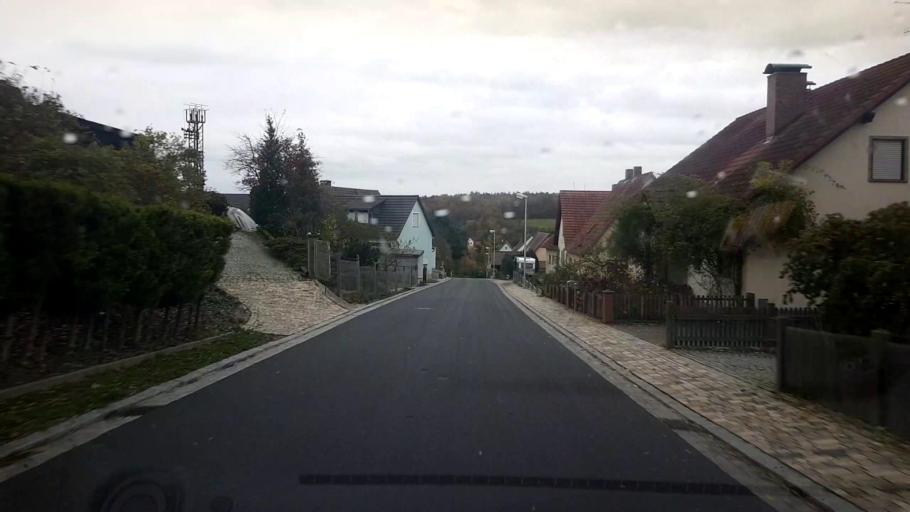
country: DE
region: Bavaria
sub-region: Upper Franconia
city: Burgwindheim
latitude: 49.8744
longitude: 10.5632
